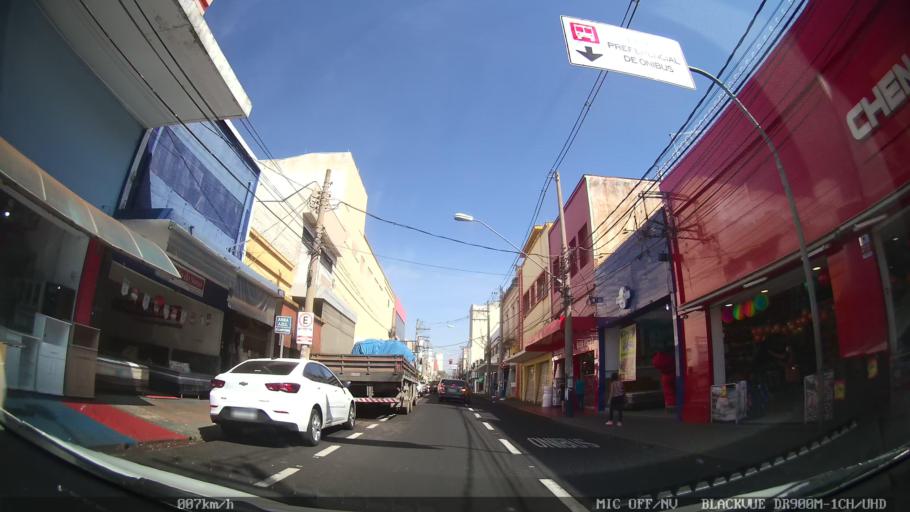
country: BR
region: Sao Paulo
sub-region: Ribeirao Preto
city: Ribeirao Preto
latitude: -21.1732
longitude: -47.8108
